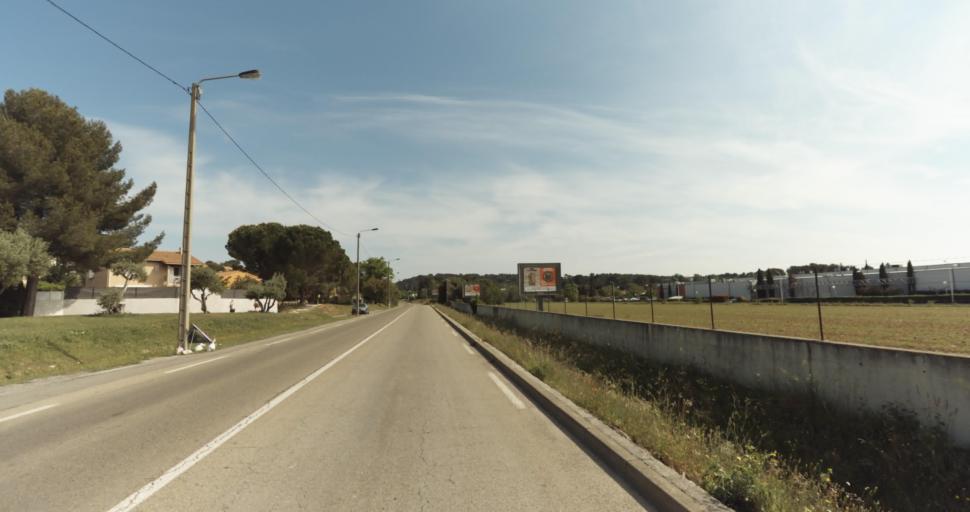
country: FR
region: Languedoc-Roussillon
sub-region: Departement du Gard
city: Rodilhan
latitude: 43.8574
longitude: 4.4015
